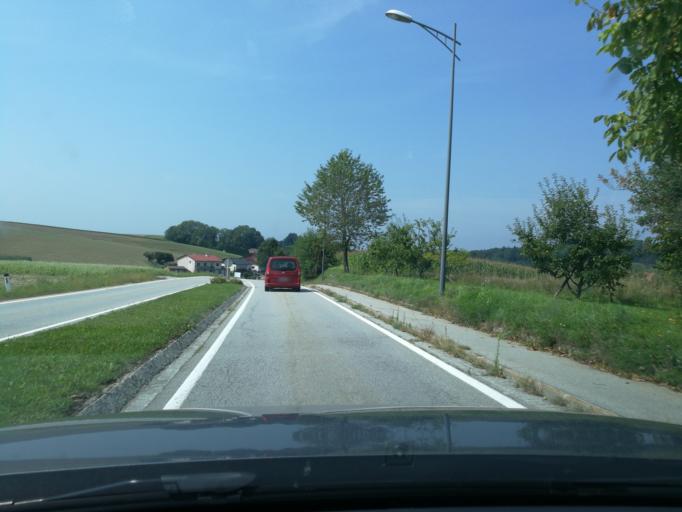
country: DE
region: Bavaria
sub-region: Lower Bavaria
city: Obernzell
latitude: 48.3621
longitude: 13.6804
